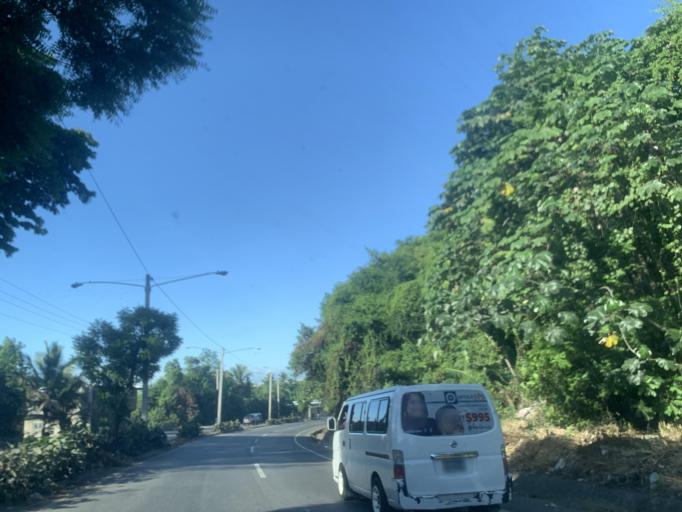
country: DO
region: San Cristobal
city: El Carril
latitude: 18.4348
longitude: -70.0198
